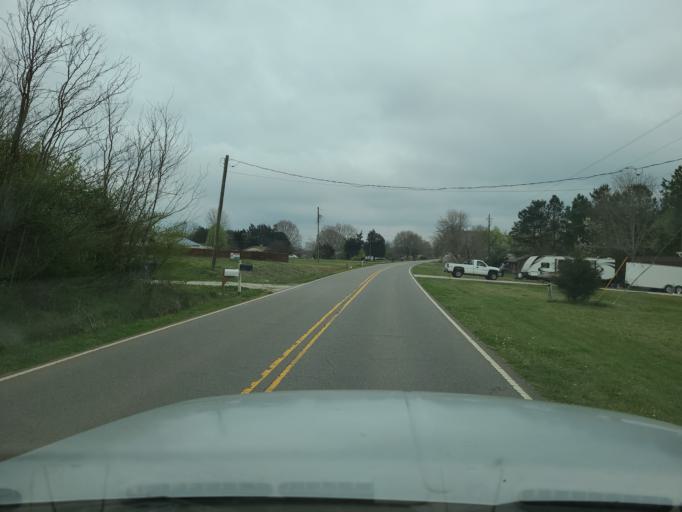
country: US
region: North Carolina
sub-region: Cleveland County
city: Shelby
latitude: 35.3775
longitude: -81.6040
